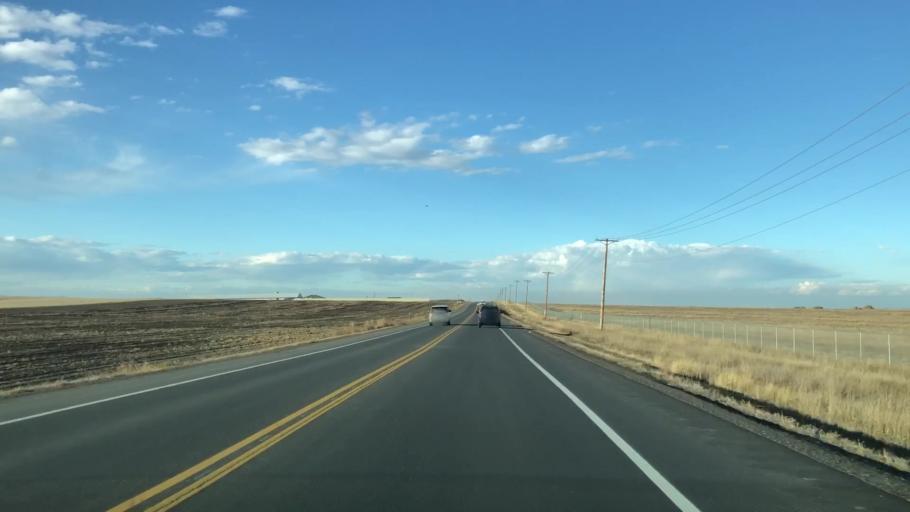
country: US
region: Colorado
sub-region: Larimer County
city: Loveland
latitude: 40.4528
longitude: -105.0205
